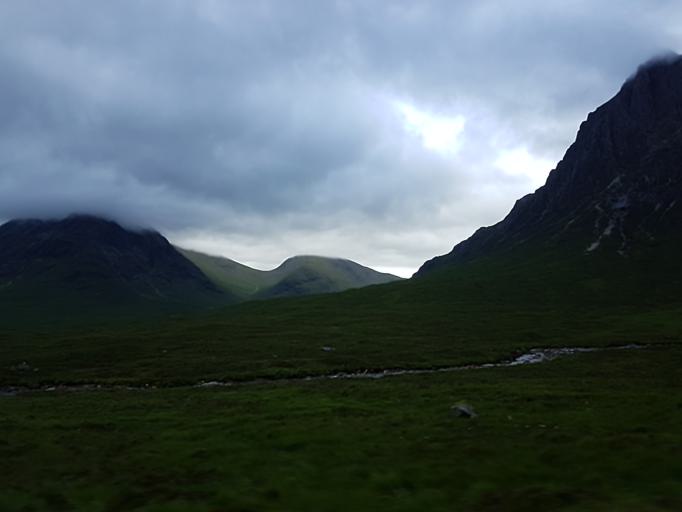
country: GB
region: Scotland
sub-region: Highland
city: Spean Bridge
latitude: 56.6566
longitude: -4.8765
